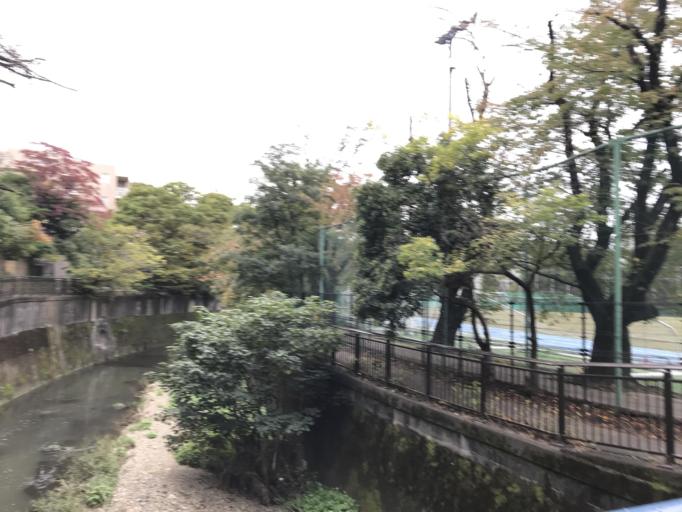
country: JP
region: Tokyo
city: Chofugaoka
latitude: 35.6449
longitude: 139.6025
